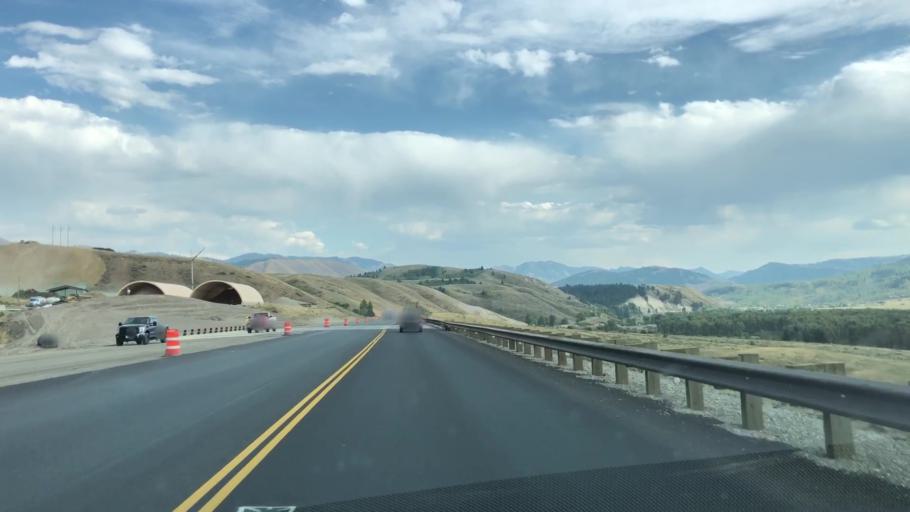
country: US
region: Wyoming
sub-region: Teton County
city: South Park
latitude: 43.4043
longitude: -110.7578
